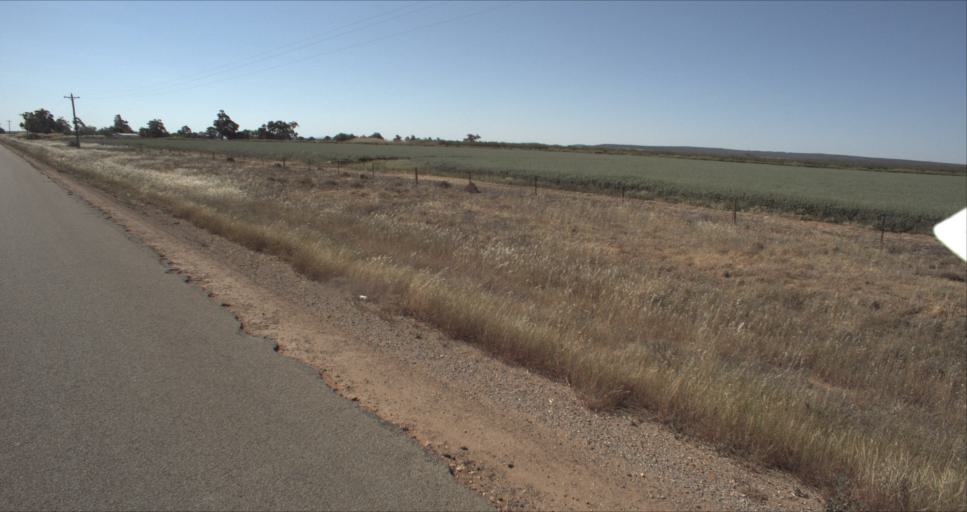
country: AU
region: New South Wales
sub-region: Leeton
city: Leeton
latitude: -34.4822
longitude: 146.3728
